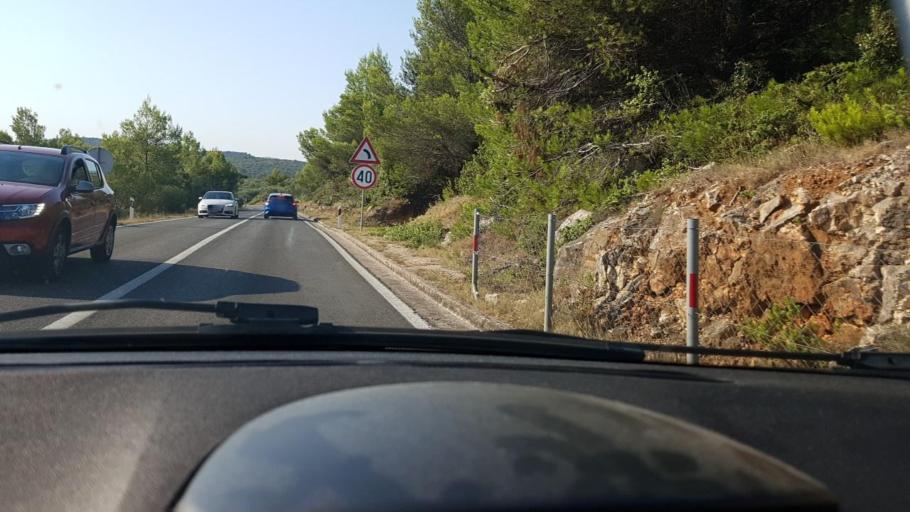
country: HR
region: Sibensko-Kniniska
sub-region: Grad Sibenik
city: Tisno
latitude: 43.7930
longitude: 15.6250
